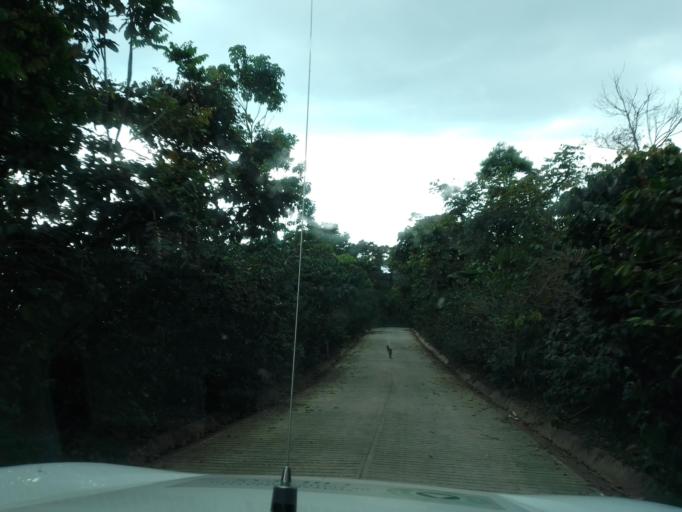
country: MX
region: Chiapas
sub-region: Union Juarez
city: Santo Domingo
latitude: 15.0661
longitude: -92.1144
